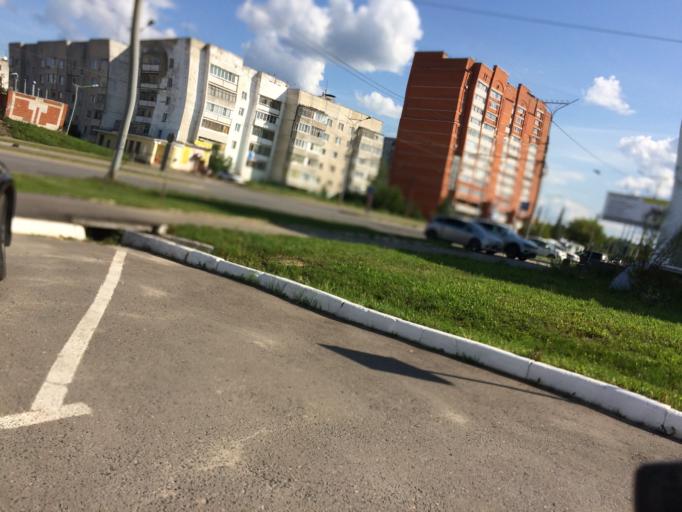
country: RU
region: Mariy-El
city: Yoshkar-Ola
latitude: 56.6261
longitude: 47.9348
